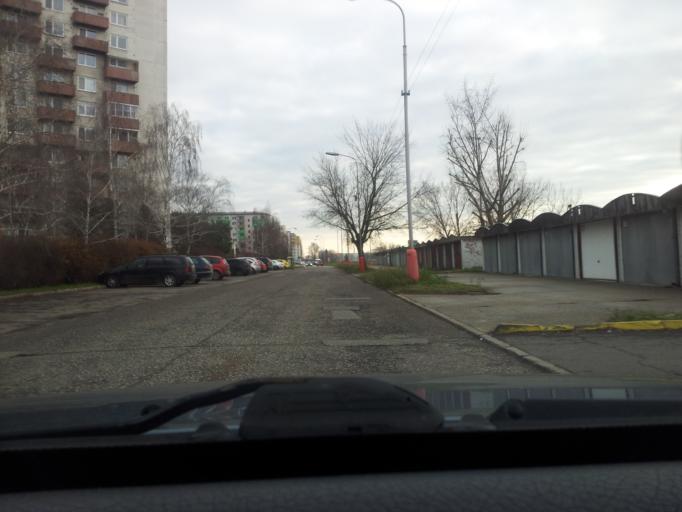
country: SK
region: Nitriansky
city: Levice
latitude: 48.2081
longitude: 18.6008
